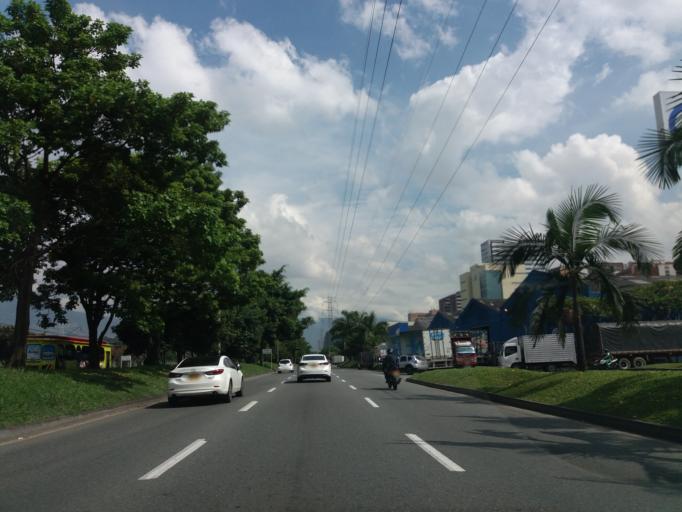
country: CO
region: Antioquia
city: Medellin
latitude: 6.2185
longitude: -75.5769
